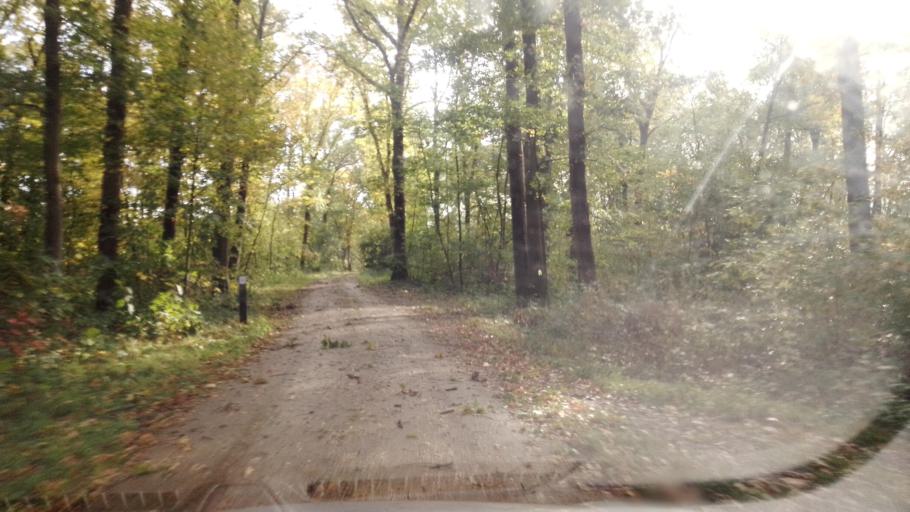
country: NL
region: Limburg
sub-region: Gemeente Venlo
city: Venlo
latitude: 51.4076
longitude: 6.1951
